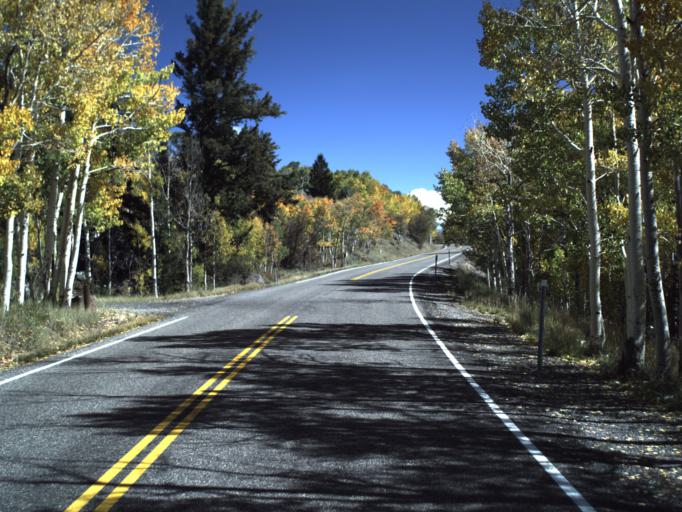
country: US
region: Utah
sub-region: Wayne County
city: Loa
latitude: 38.5445
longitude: -111.7298
